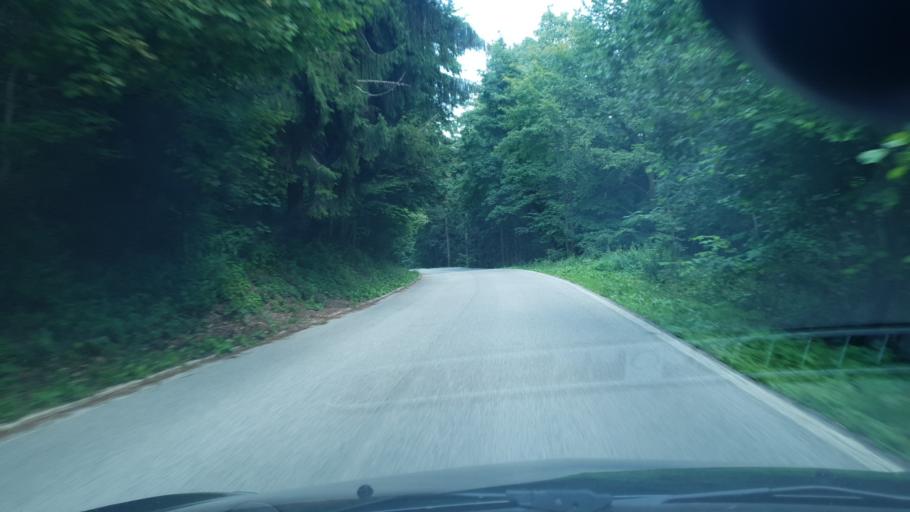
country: HR
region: Grad Zagreb
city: Kasina
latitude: 45.9048
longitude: 15.9702
